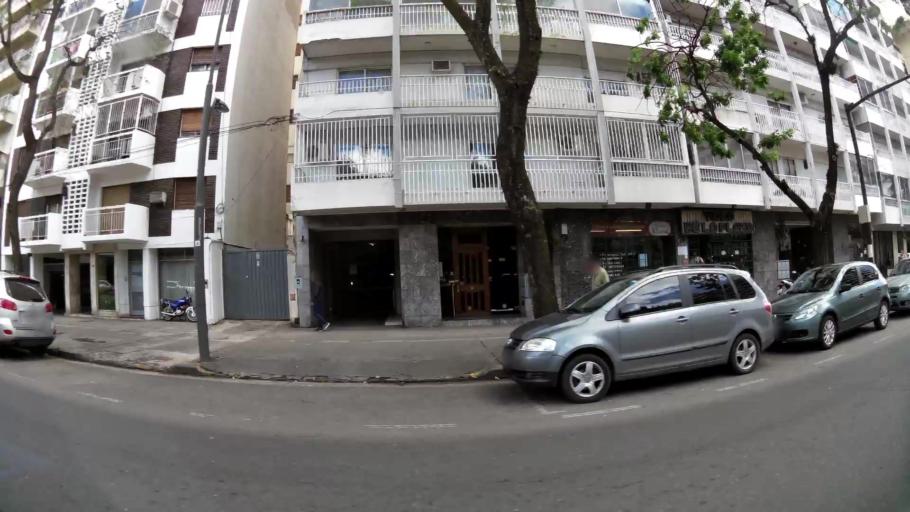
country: AR
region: Santa Fe
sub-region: Departamento de Rosario
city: Rosario
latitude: -32.9581
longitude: -60.6359
